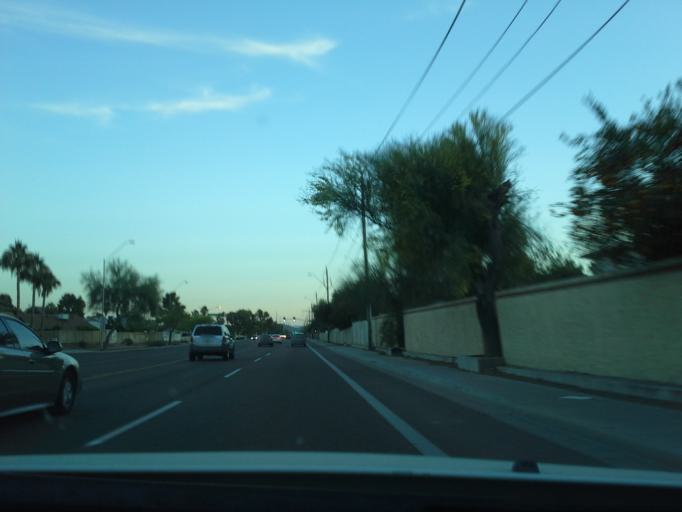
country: US
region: Arizona
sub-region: Maricopa County
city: Glendale
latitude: 33.6638
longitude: -112.0658
